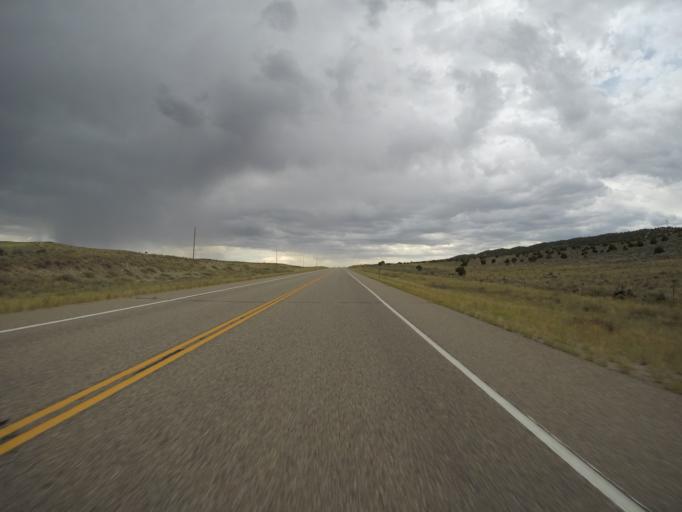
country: US
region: Colorado
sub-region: Rio Blanco County
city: Rangely
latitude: 40.3585
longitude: -108.4374
